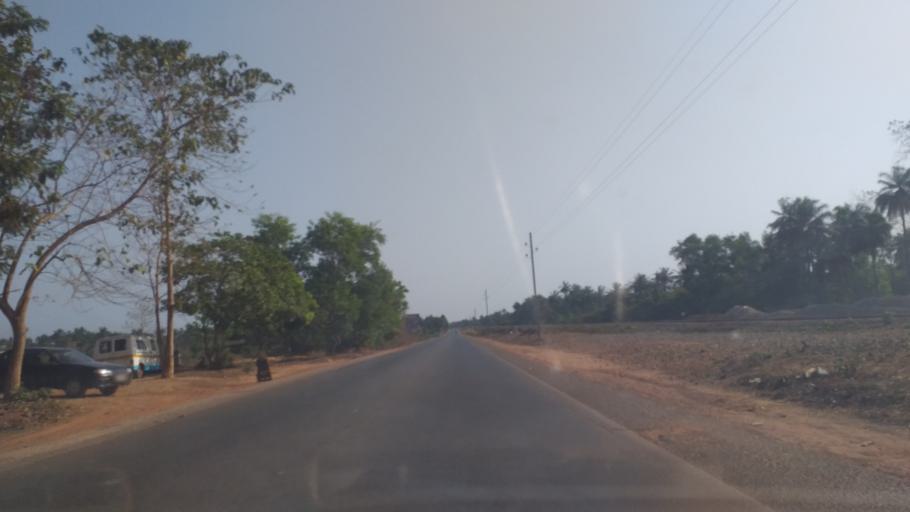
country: GN
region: Boke
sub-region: Boke Prefecture
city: Kamsar
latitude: 10.7461
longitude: -14.5101
